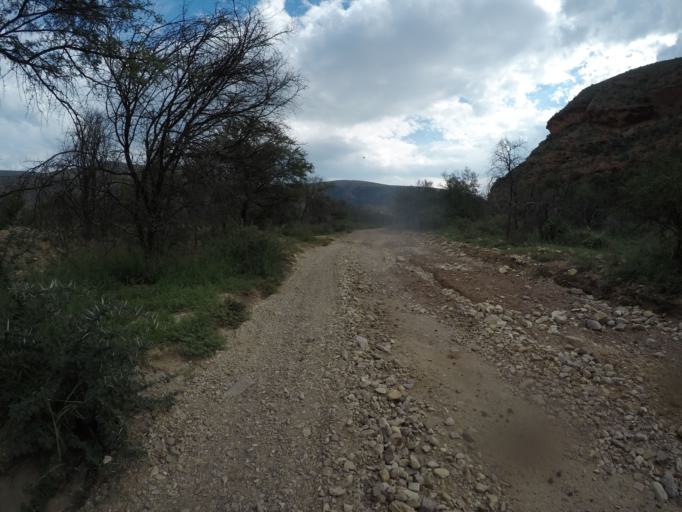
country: ZA
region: Eastern Cape
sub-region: Cacadu District Municipality
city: Kareedouw
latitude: -33.6034
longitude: 24.2046
